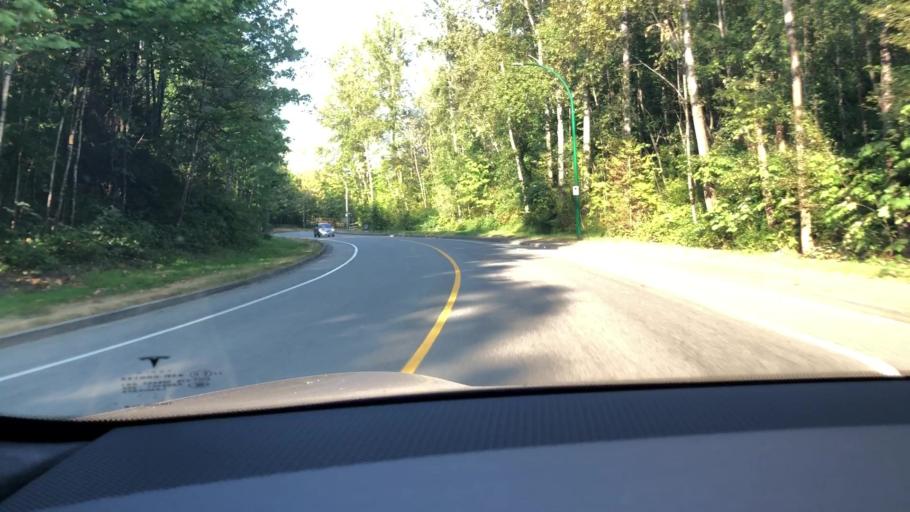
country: CA
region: British Columbia
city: Burnaby
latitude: 49.2288
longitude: -122.9783
